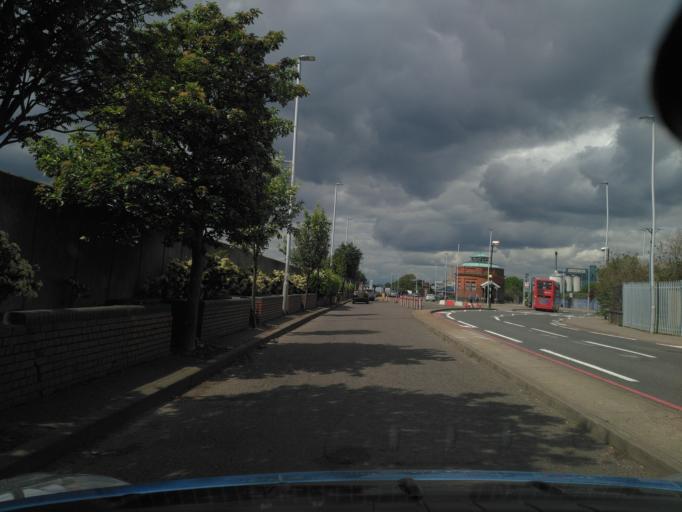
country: GB
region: England
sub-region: Greater London
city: Woolwich
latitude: 51.4988
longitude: 0.0632
